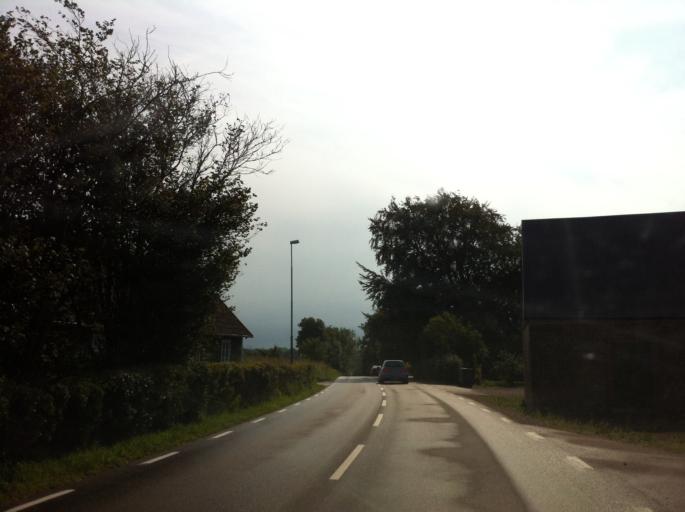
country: SE
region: Skane
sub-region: Helsingborg
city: Barslov
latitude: 55.9807
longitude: 12.8564
